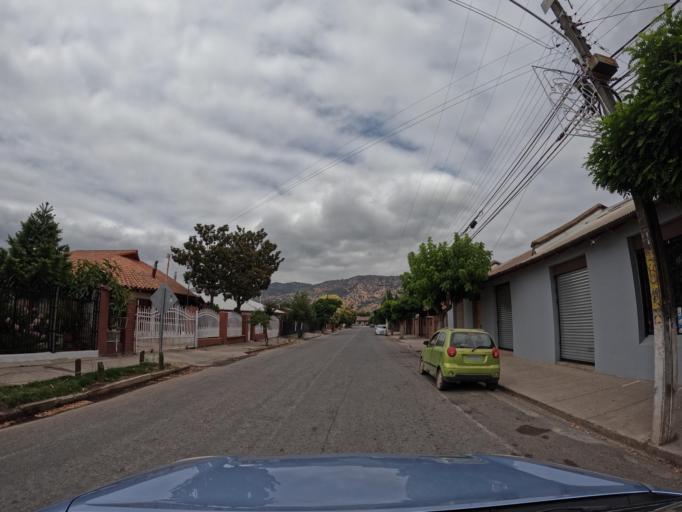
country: CL
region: Maule
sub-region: Provincia de Curico
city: Teno
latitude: -34.7622
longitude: -71.1964
